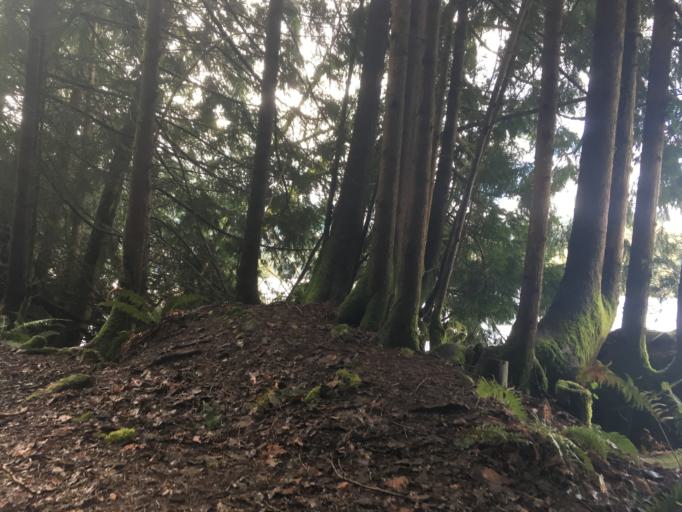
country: US
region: Washington
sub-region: Whatcom County
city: Sudden Valley
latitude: 48.7132
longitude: -122.2979
